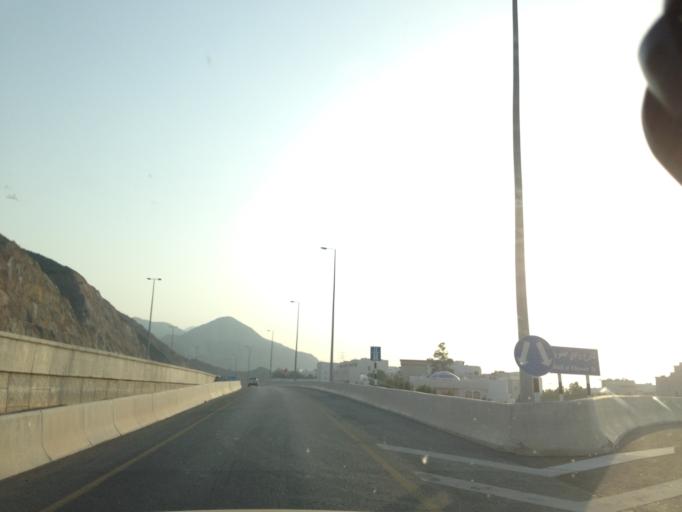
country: OM
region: Muhafazat Masqat
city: Bawshar
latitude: 23.5892
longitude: 58.4590
